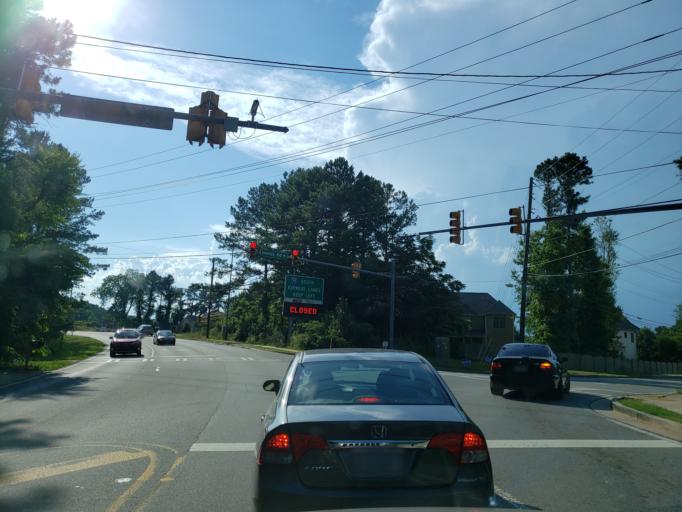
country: US
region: Georgia
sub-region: Cobb County
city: Kennesaw
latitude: 34.0644
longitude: -84.6056
